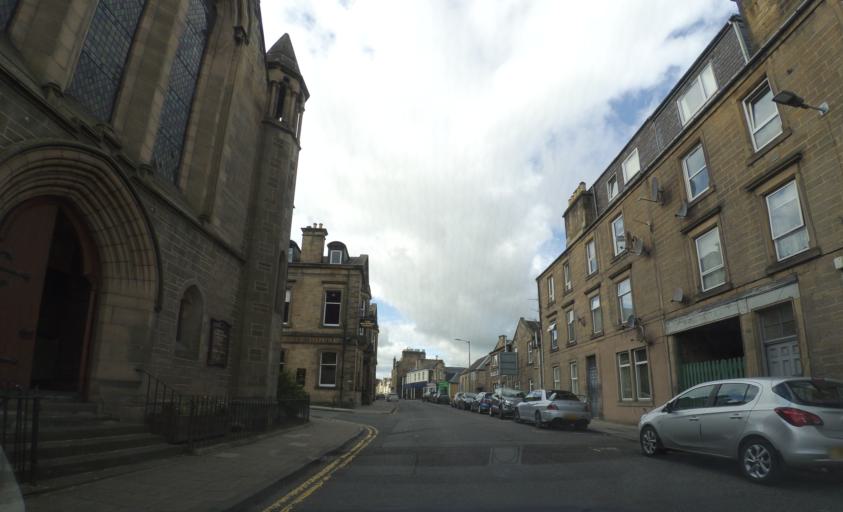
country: GB
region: Scotland
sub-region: The Scottish Borders
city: Hawick
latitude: 55.4257
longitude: -2.7830
